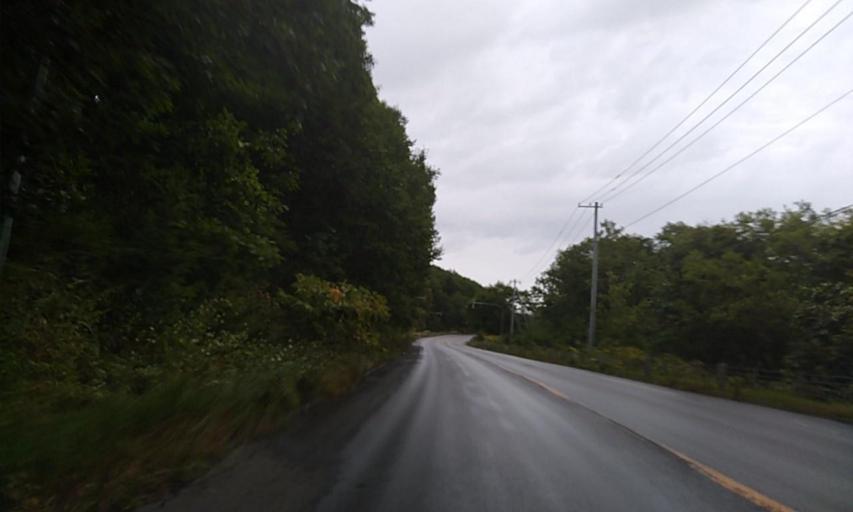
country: JP
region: Hokkaido
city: Mombetsu
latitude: 44.4879
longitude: 143.0833
